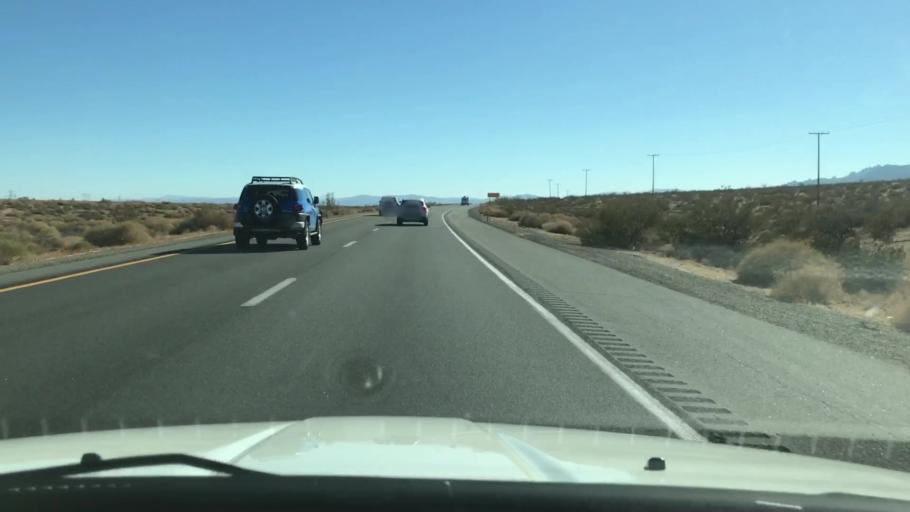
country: US
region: California
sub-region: Kern County
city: Inyokern
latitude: 35.8605
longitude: -117.8776
